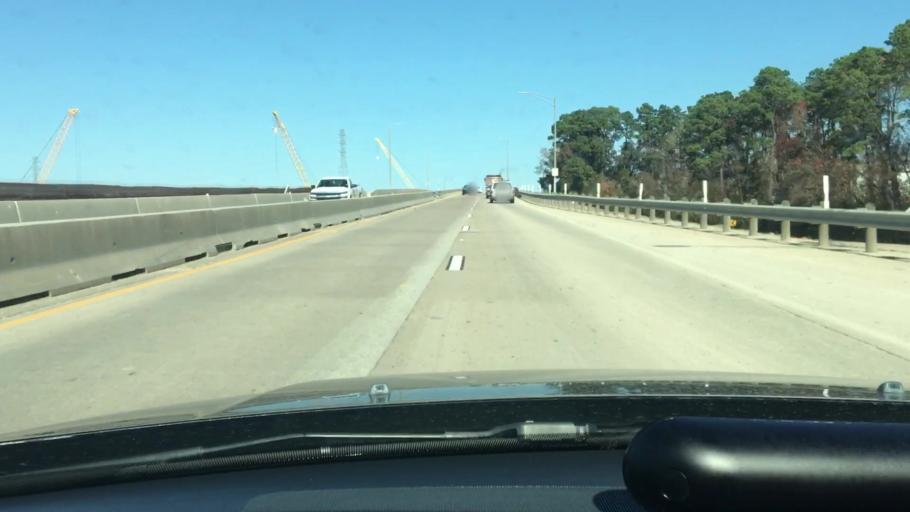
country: US
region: Texas
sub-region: Harris County
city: Cloverleaf
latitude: 29.7522
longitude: -95.1458
